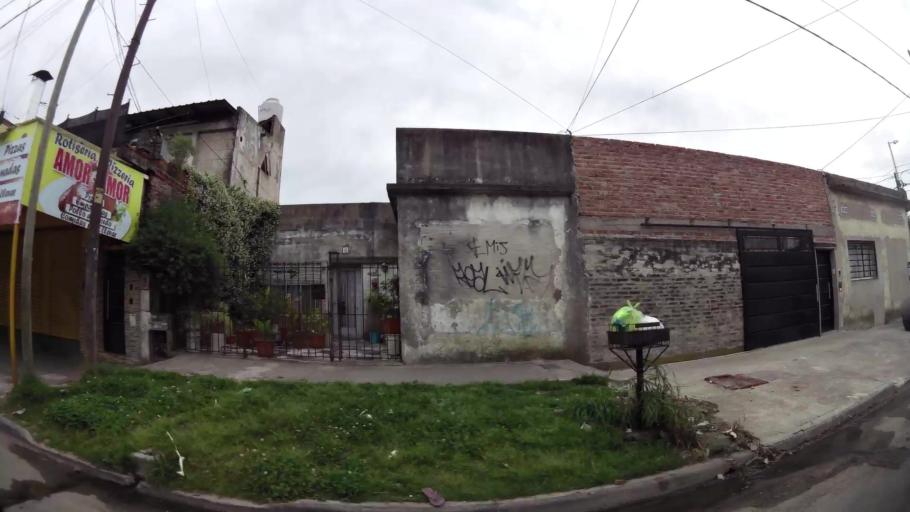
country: AR
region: Buenos Aires
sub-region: Partido de Lanus
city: Lanus
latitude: -34.6913
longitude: -58.3698
